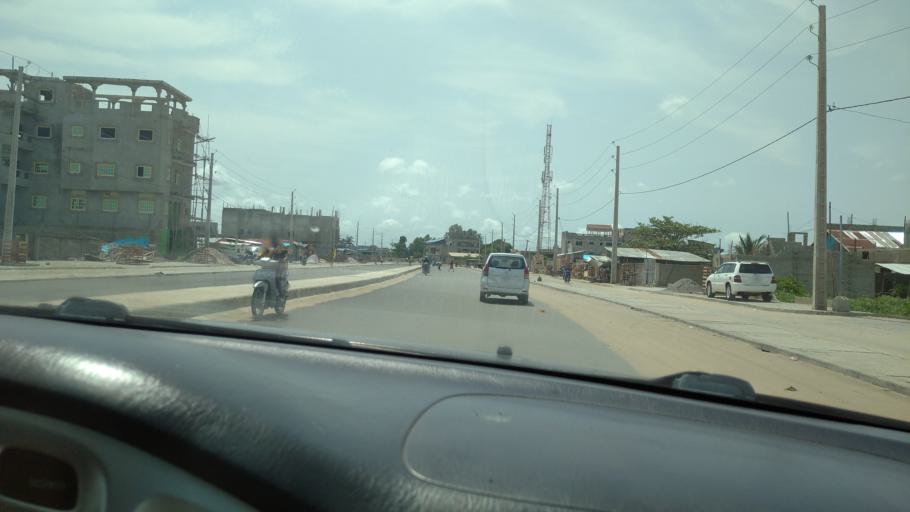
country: BJ
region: Littoral
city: Cotonou
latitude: 6.3728
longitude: 2.4988
